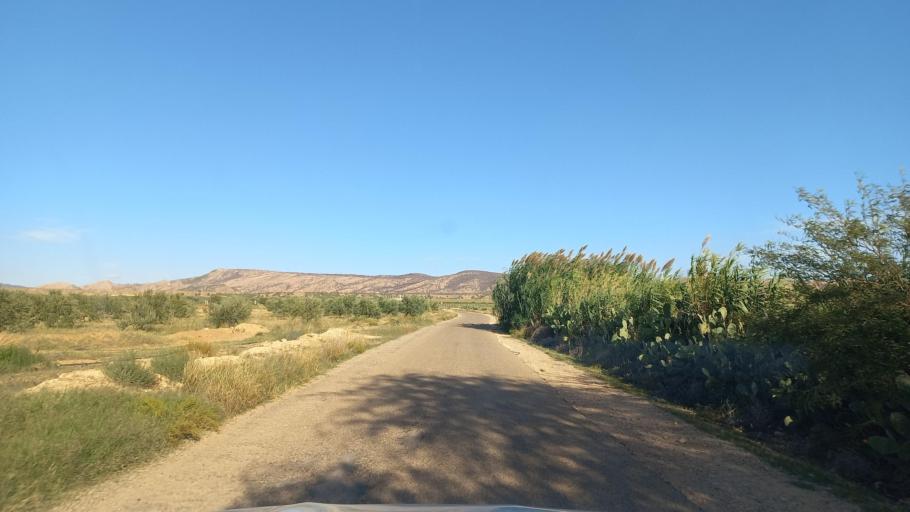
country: TN
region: Al Qasrayn
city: Sbiba
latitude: 35.3369
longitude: 9.1142
